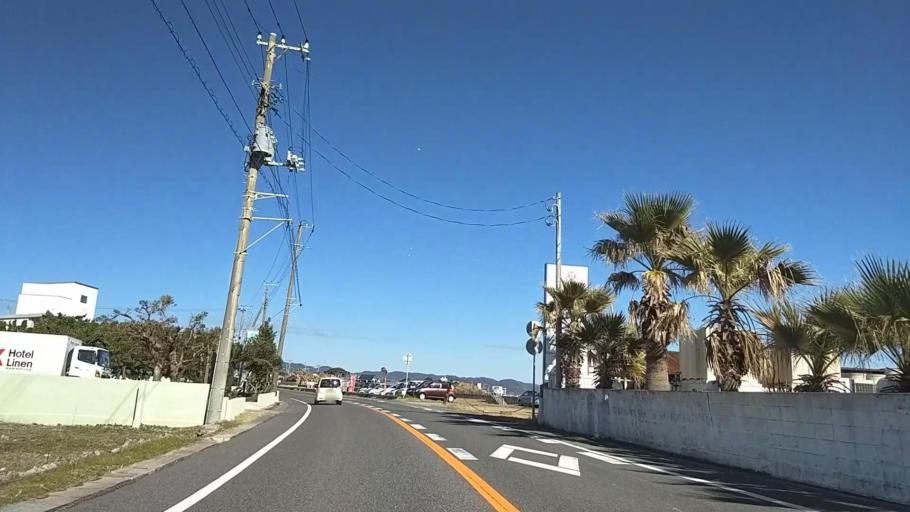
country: JP
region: Chiba
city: Tateyama
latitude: 34.9787
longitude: 139.9664
